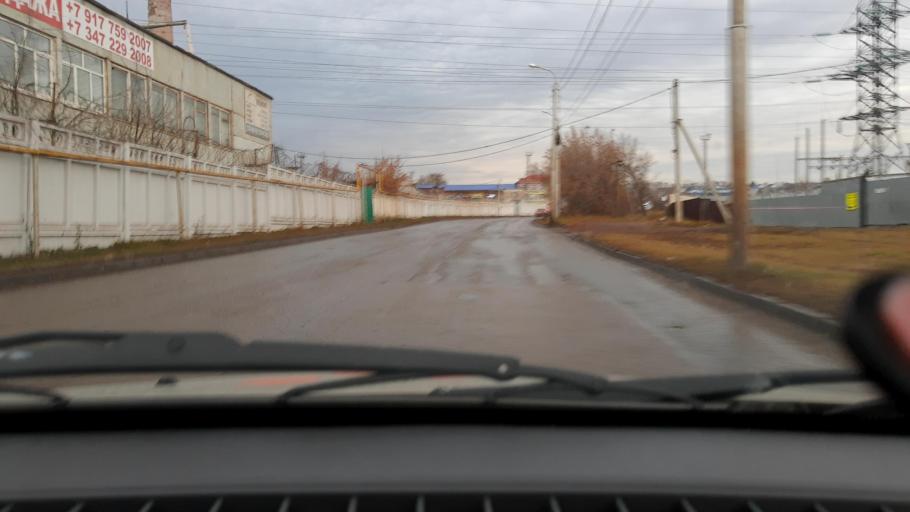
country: RU
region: Bashkortostan
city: Avdon
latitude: 54.6860
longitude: 55.8116
